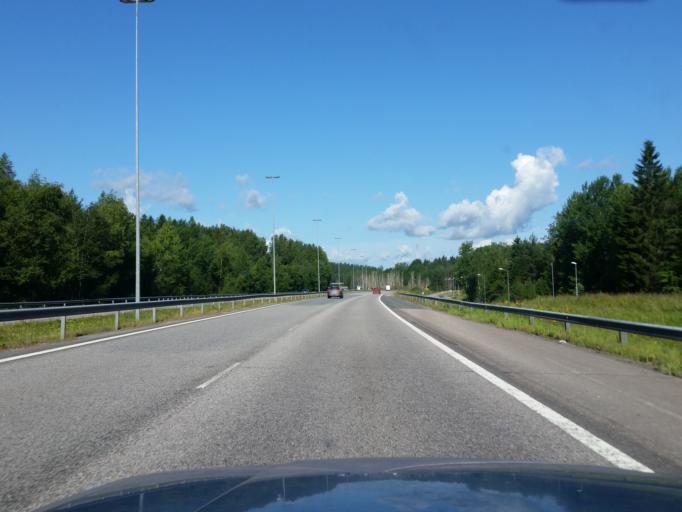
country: FI
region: Uusimaa
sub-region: Helsinki
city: Kirkkonummi
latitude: 60.2824
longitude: 24.4377
